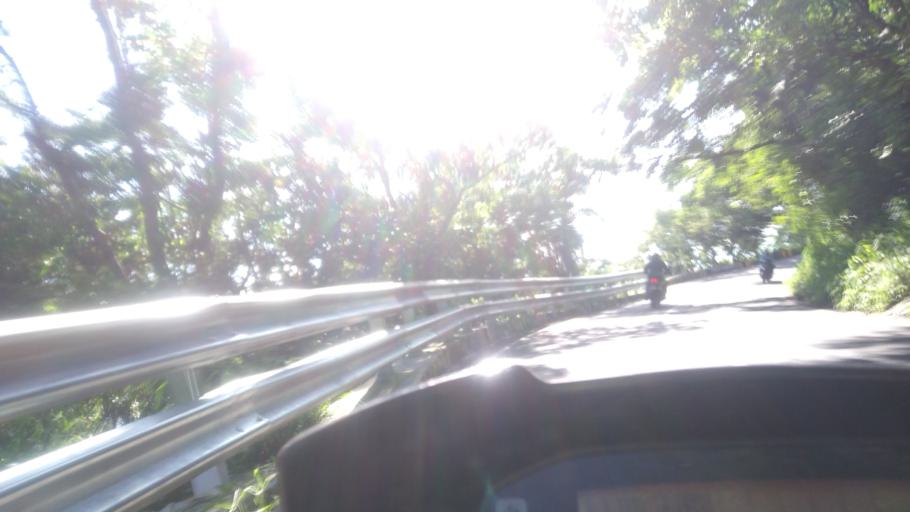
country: IN
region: Tamil Nadu
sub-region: Salem
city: Salem
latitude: 11.7559
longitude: 78.1892
